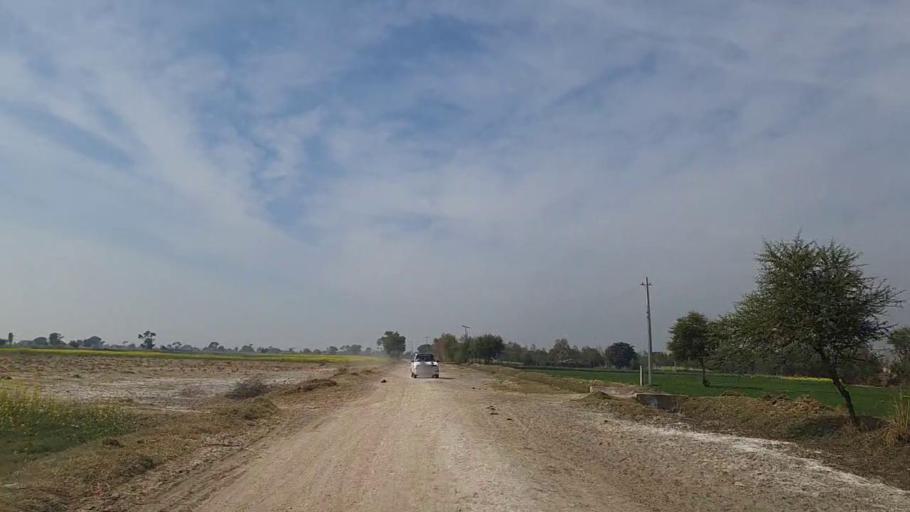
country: PK
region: Sindh
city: Nawabshah
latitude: 26.3277
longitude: 68.4276
